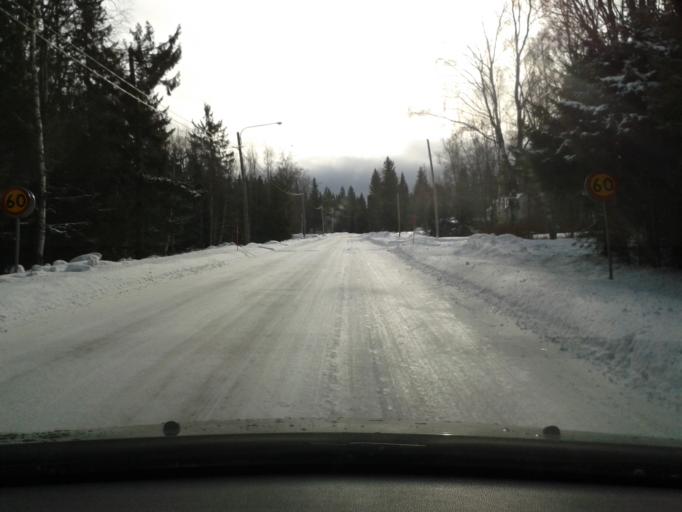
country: SE
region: Vaesterbotten
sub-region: Vilhelmina Kommun
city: Sjoberg
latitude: 64.6977
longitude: 16.2643
